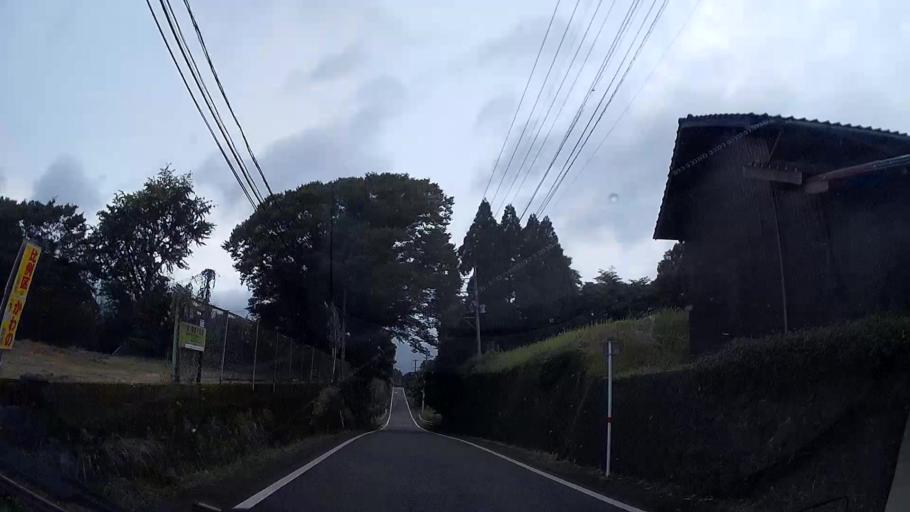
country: JP
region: Kumamoto
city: Aso
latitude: 32.8424
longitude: 131.0335
